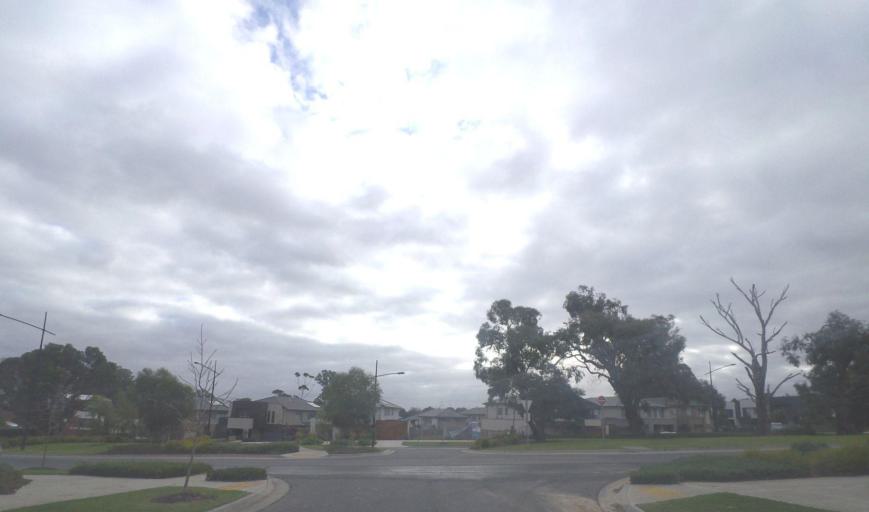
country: AU
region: Victoria
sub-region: Manningham
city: Doncaster
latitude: -37.7845
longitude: 145.1164
